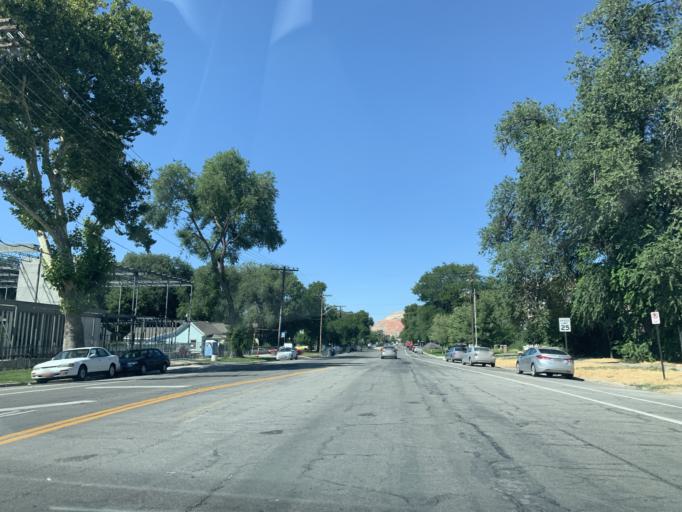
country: US
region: Utah
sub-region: Salt Lake County
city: Salt Lake City
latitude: 40.7720
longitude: -111.9082
